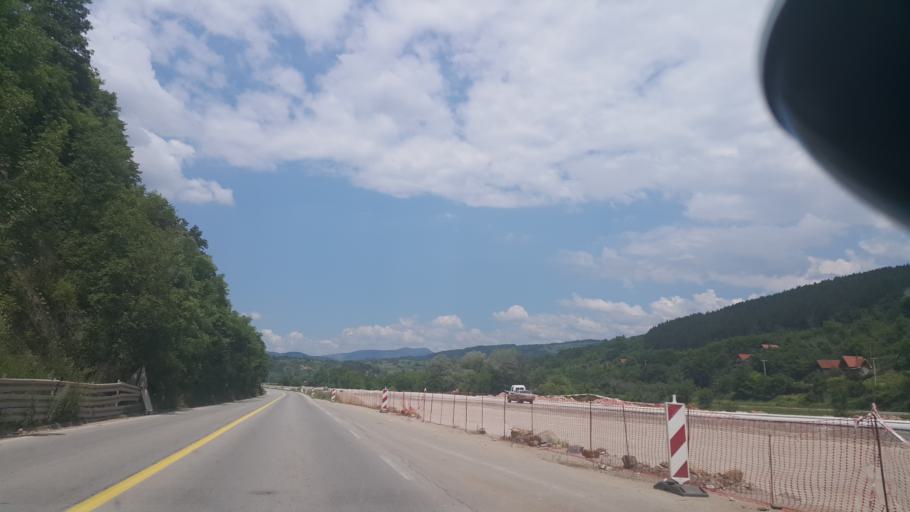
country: RS
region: Central Serbia
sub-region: Pirotski Okrug
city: Pirot
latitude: 43.2000
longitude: 22.5586
